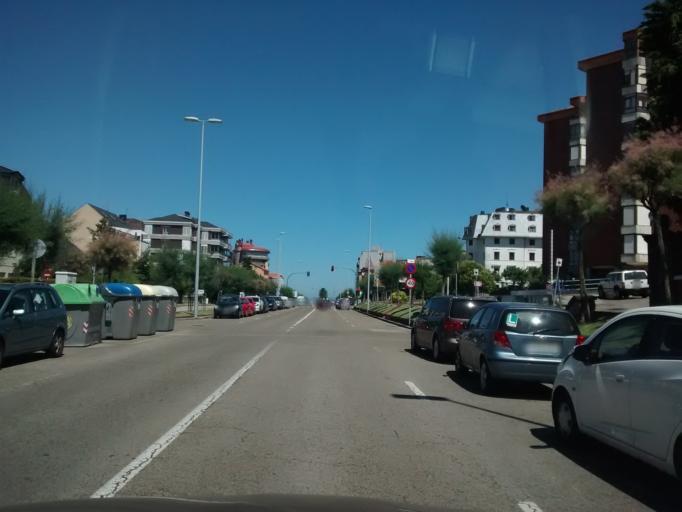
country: ES
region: Cantabria
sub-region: Provincia de Cantabria
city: Santander
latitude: 43.4730
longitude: -3.7899
